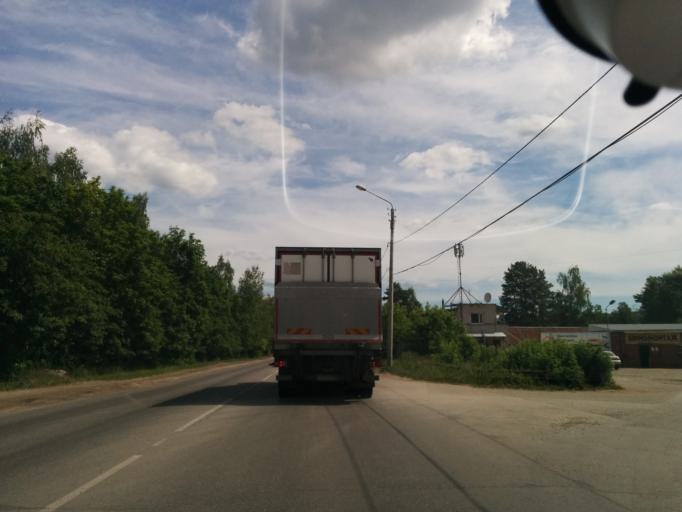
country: RU
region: Perm
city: Overyata
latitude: 58.0161
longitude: 55.9619
